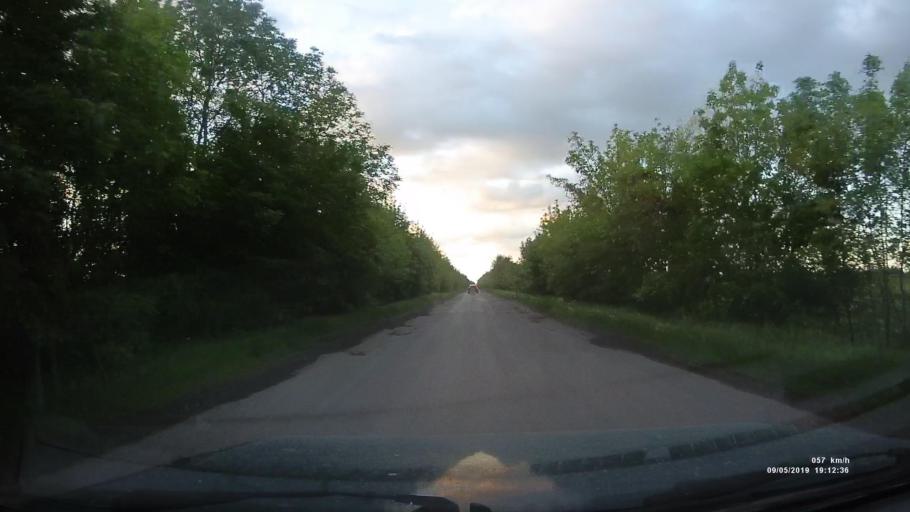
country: RU
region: Krasnodarskiy
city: Kanelovskaya
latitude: 46.7430
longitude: 39.2137
